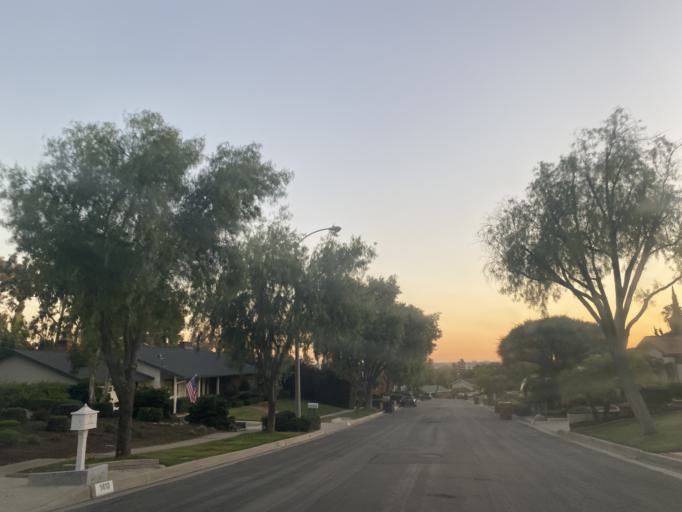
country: US
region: California
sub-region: Orange County
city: Fullerton
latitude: 33.8850
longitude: -117.9045
